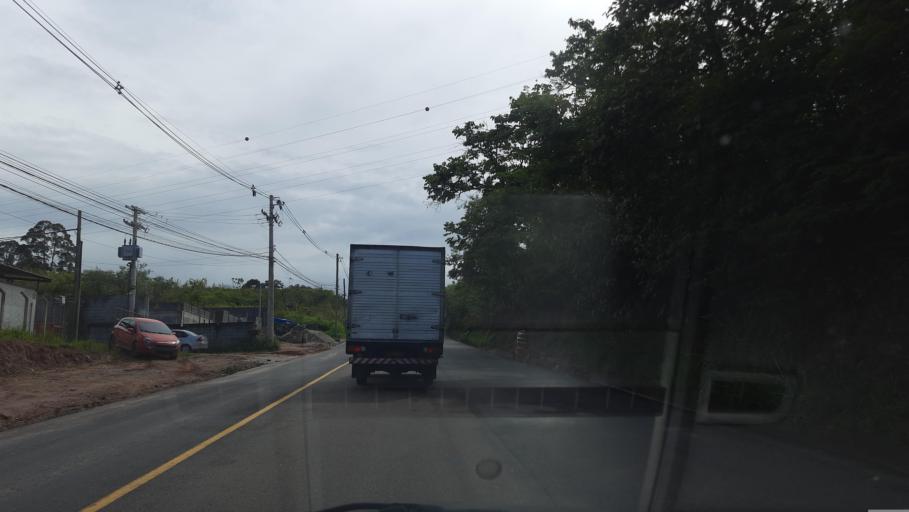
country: BR
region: Sao Paulo
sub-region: Caieiras
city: Caieiras
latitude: -23.3711
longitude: -46.6876
